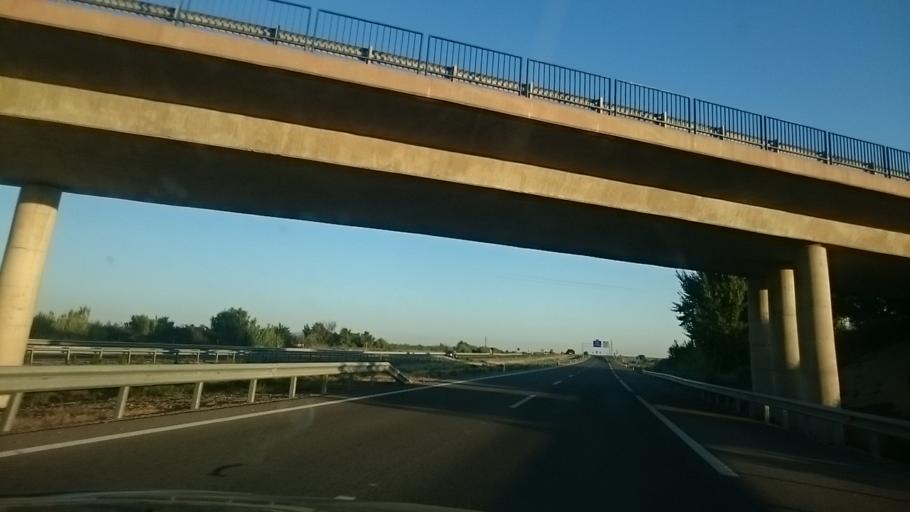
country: ES
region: Navarre
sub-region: Provincia de Navarra
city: Murchante
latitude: 42.0246
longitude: -1.6241
